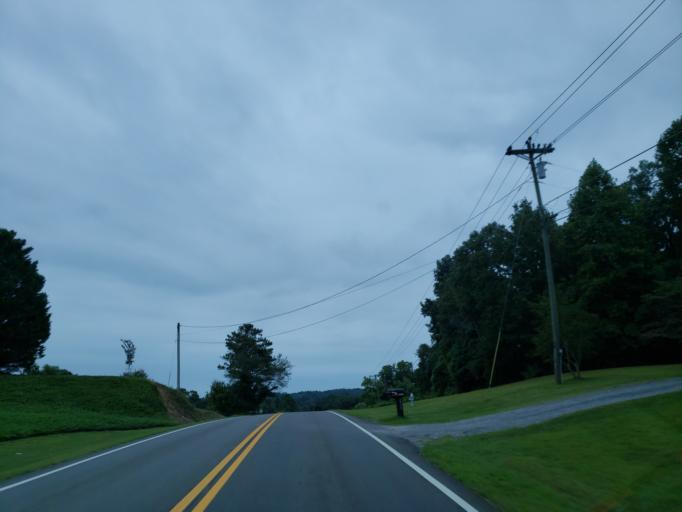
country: US
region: Georgia
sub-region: Cherokee County
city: Canton
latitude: 34.3158
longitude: -84.4642
